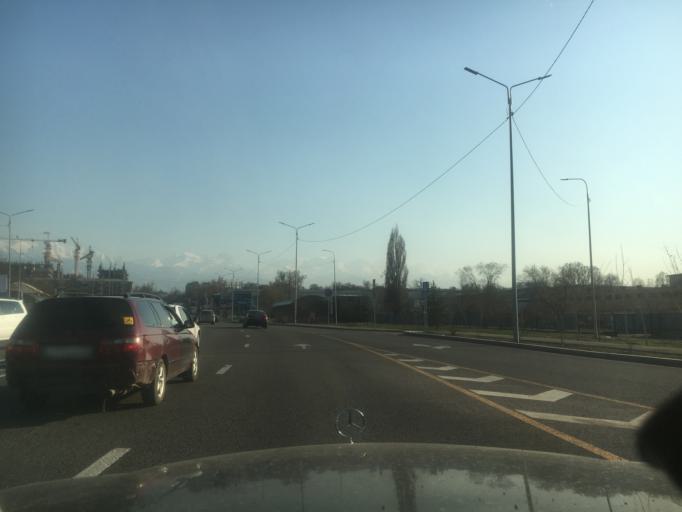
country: KZ
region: Almaty Qalasy
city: Almaty
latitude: 43.2732
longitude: 76.9446
